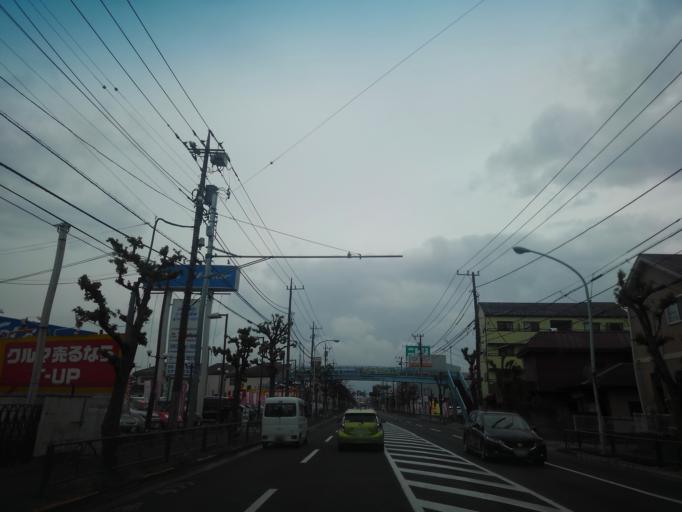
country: JP
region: Tokyo
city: Tanashicho
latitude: 35.7351
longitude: 139.5260
